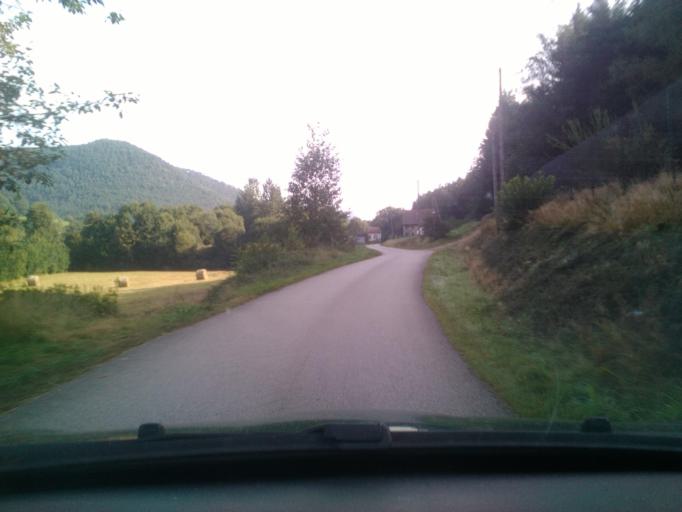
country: FR
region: Lorraine
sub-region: Departement des Vosges
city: Taintrux
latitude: 48.2664
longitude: 6.8880
